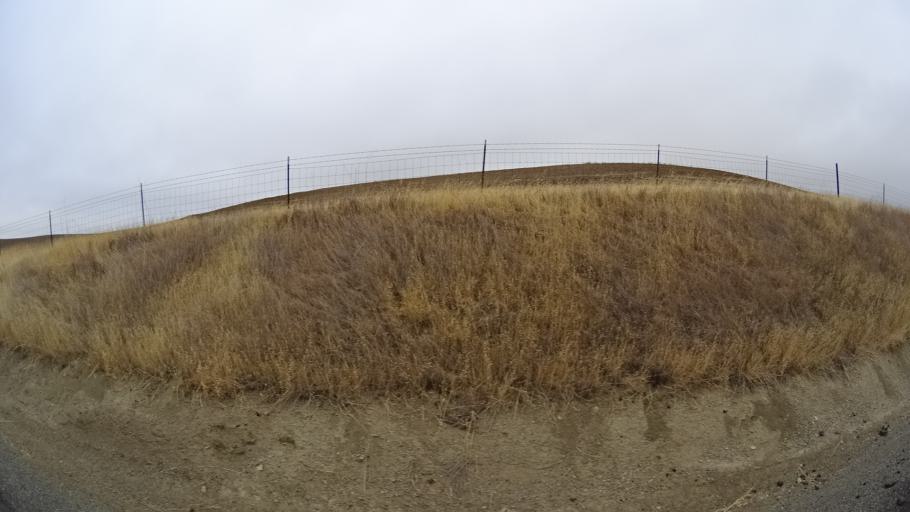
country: US
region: California
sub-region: Yolo County
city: Dunnigan
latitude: 38.8842
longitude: -122.0121
